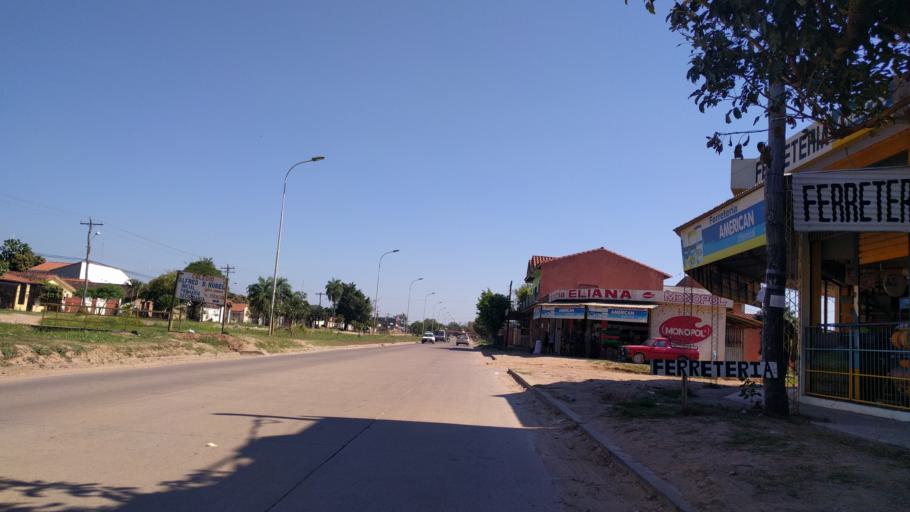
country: BO
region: Santa Cruz
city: Santa Cruz de la Sierra
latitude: -17.8540
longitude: -63.1947
